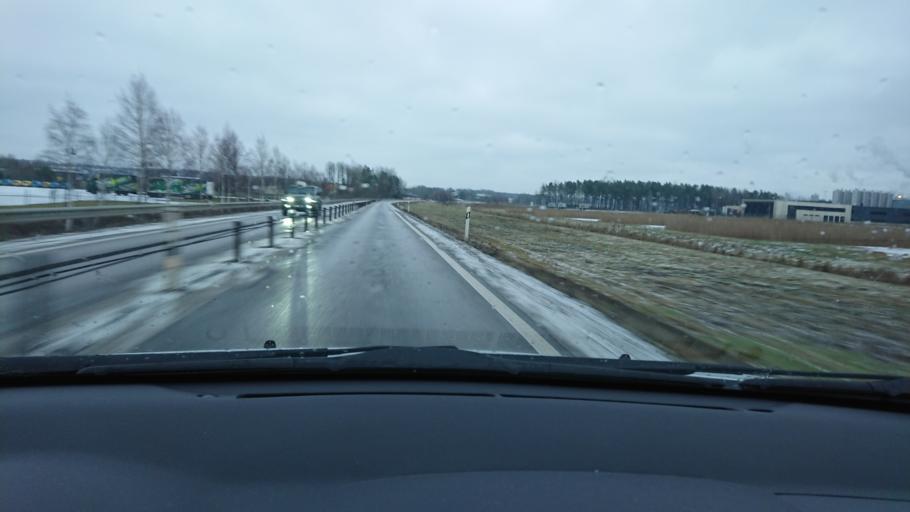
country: SE
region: Kalmar
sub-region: Vimmerby Kommun
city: Vimmerby
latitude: 57.6527
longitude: 15.8490
